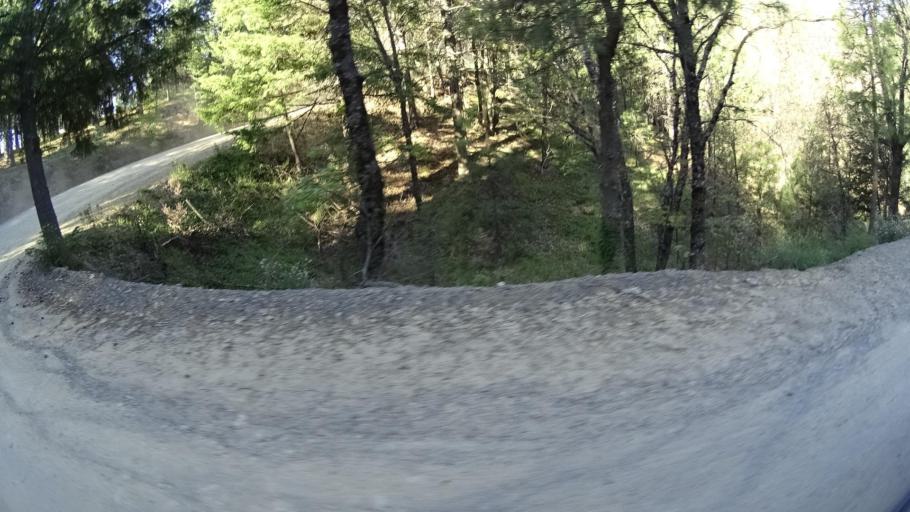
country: US
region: California
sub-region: Lake County
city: Upper Lake
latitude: 39.3182
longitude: -122.9442
